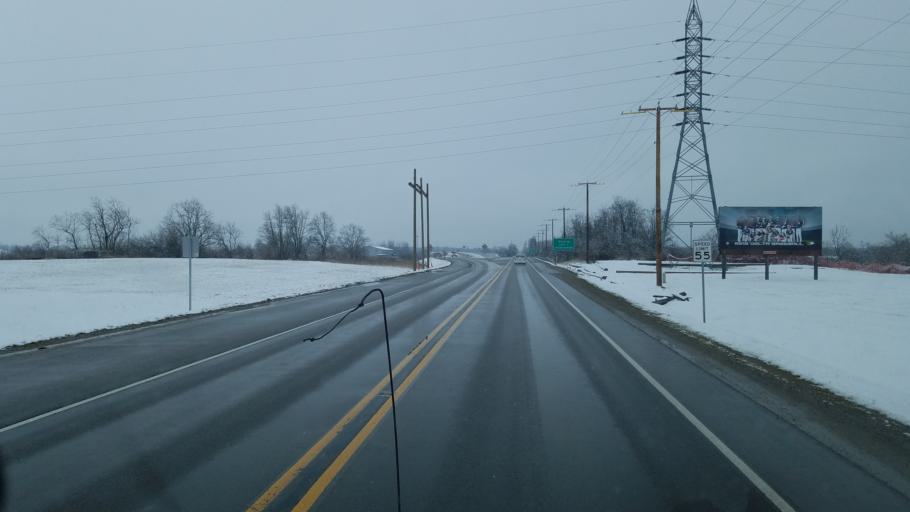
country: US
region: Indiana
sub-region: Delaware County
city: Muncie
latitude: 40.2550
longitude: -85.3680
